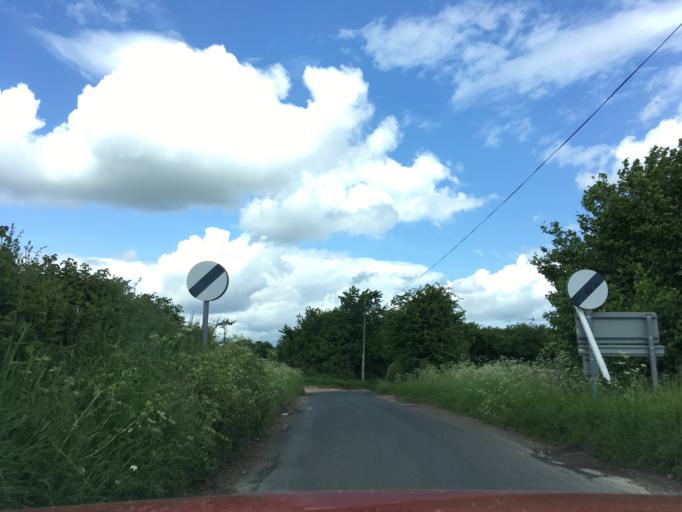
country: GB
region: England
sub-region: Gloucestershire
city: Shurdington
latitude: 51.8151
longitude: -2.0880
